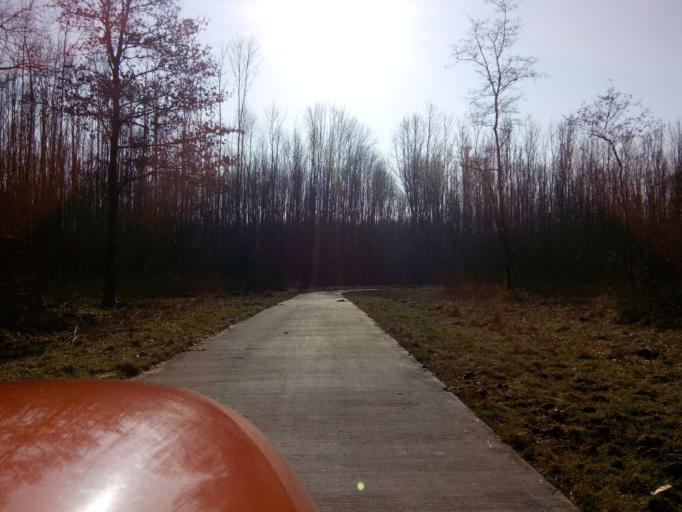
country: NL
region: Flevoland
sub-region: Gemeente Zeewolde
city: Zeewolde
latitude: 52.2904
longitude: 5.4911
